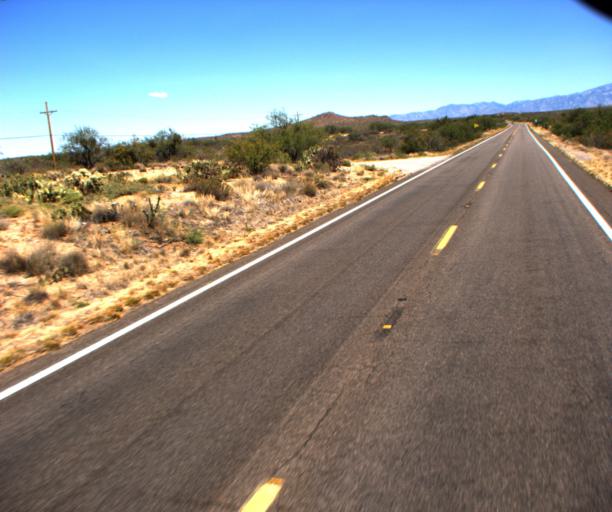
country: US
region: Arizona
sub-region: Pima County
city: Catalina
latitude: 32.6607
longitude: -111.0475
